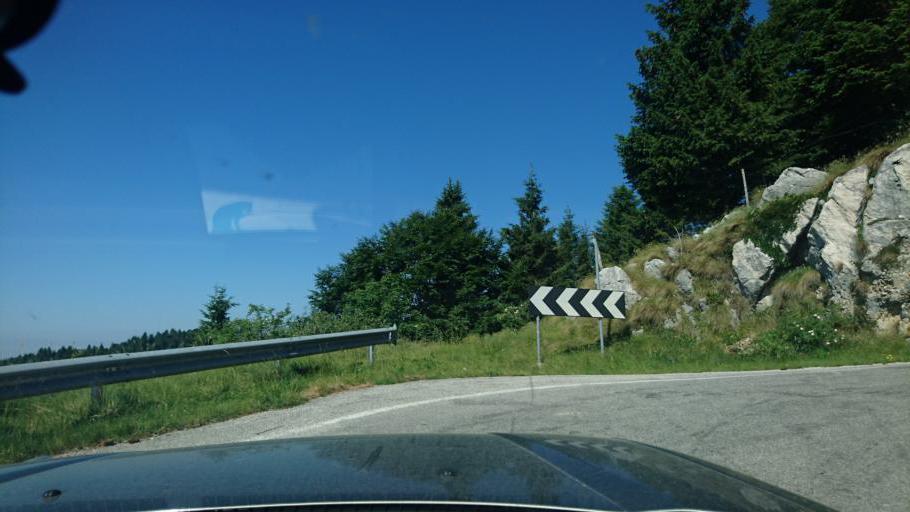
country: IT
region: Veneto
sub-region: Provincia di Treviso
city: Crespano del Grappa
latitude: 45.8542
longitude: 11.7971
